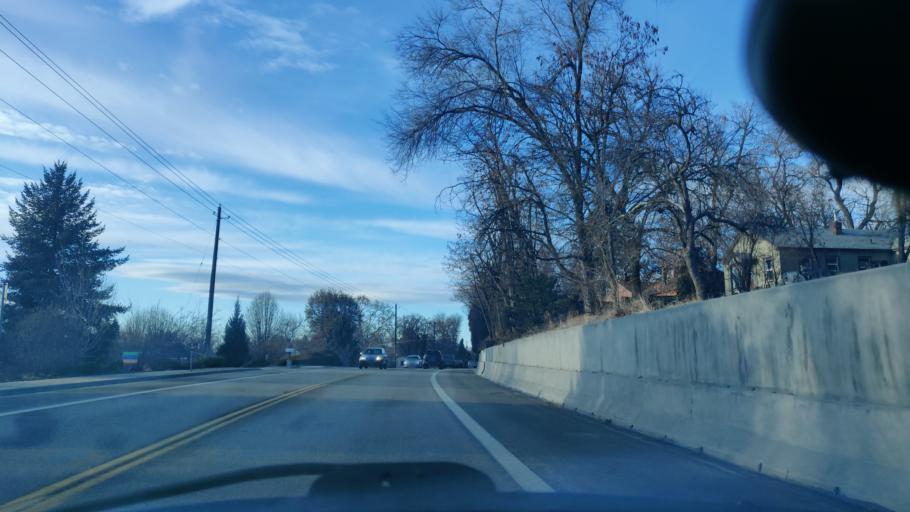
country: US
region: Idaho
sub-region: Ada County
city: Garden City
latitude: 43.6490
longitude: -116.2235
